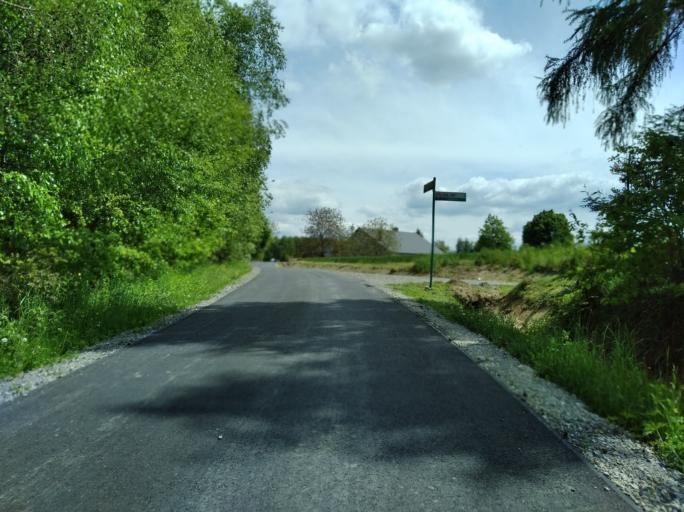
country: PL
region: Subcarpathian Voivodeship
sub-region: Powiat ropczycko-sedziszowski
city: Wielopole Skrzynskie
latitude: 49.9076
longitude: 21.6006
